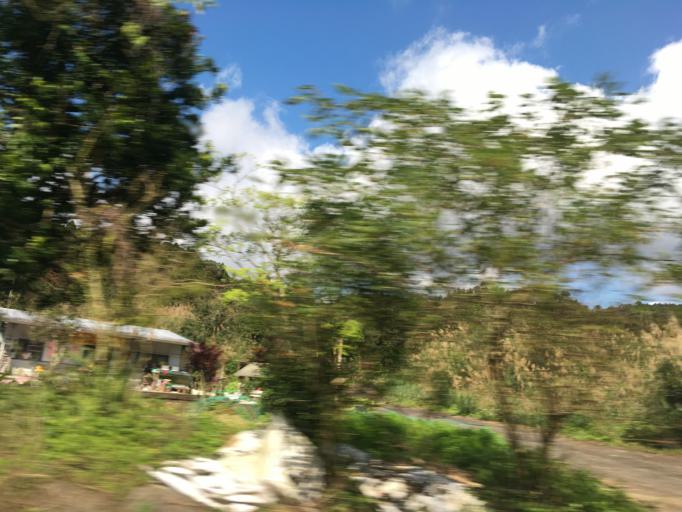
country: TW
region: Taiwan
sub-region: Yilan
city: Yilan
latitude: 24.7505
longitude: 121.6302
